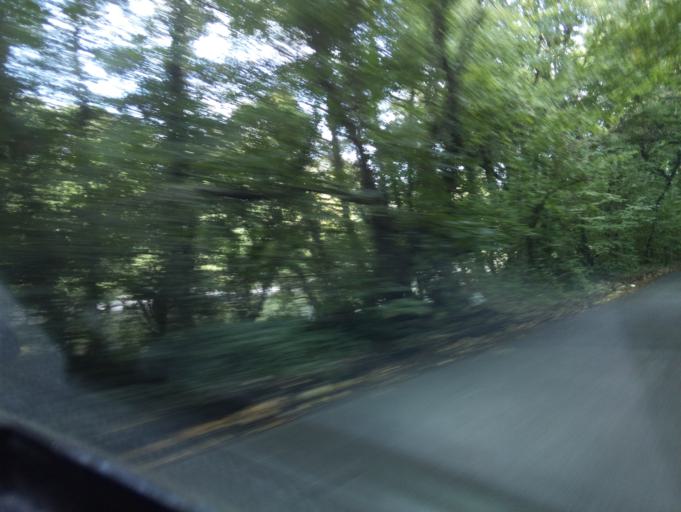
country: GB
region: Wales
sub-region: Caerphilly County Borough
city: Abertridwr
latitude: 51.5666
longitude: -3.2877
